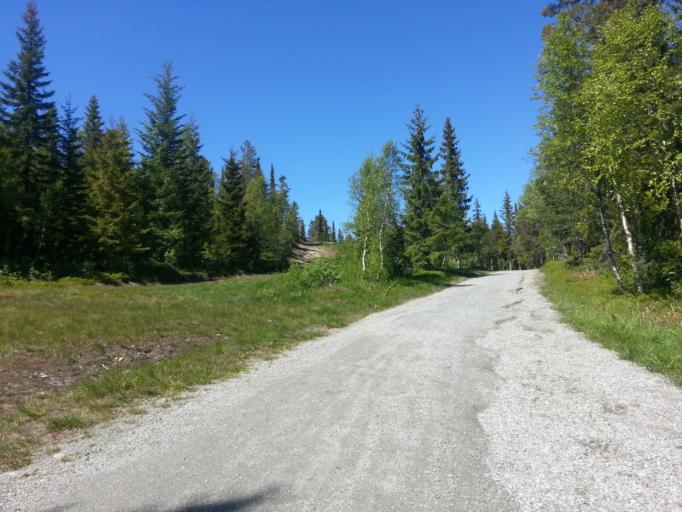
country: NO
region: Sor-Trondelag
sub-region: Trondheim
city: Trondheim
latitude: 63.4107
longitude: 10.2843
